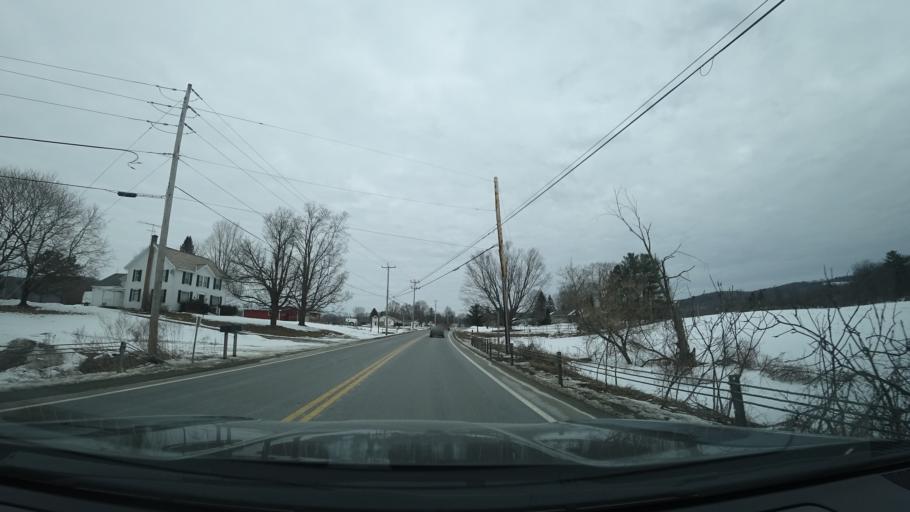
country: US
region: New York
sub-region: Washington County
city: Cambridge
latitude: 43.1586
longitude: -73.3386
